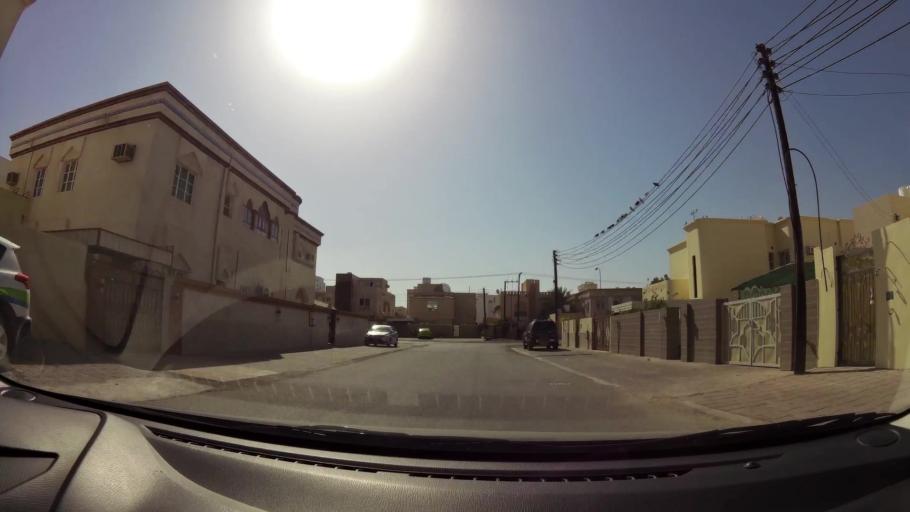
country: OM
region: Muhafazat Masqat
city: As Sib al Jadidah
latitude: 23.6297
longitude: 58.2010
